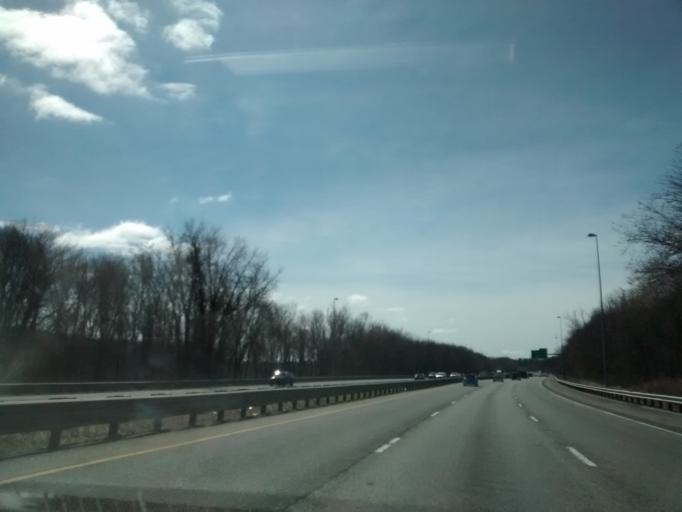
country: US
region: Massachusetts
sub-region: Worcester County
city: Auburn
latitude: 42.2192
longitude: -71.8291
